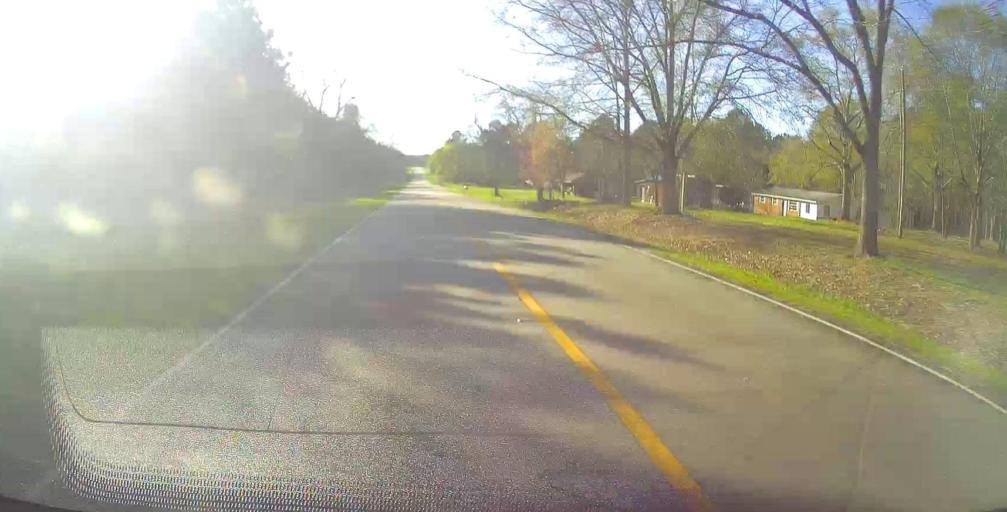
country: US
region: Georgia
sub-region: Houston County
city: Perry
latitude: 32.3738
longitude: -83.7130
